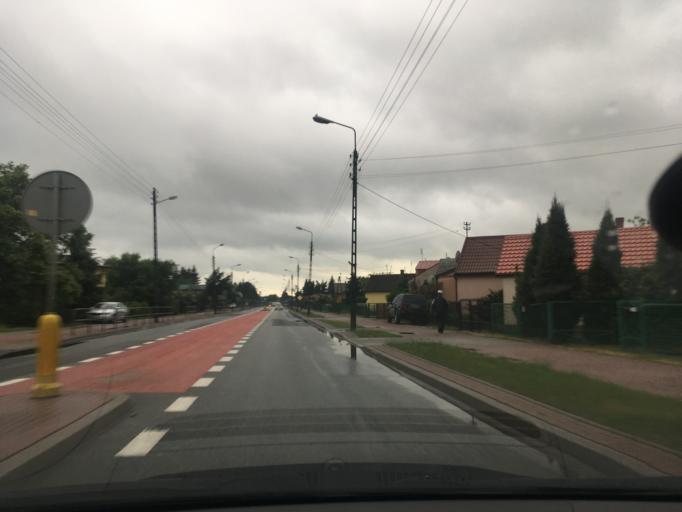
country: PL
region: Lublin Voivodeship
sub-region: Powiat rycki
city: Deblin
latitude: 51.5671
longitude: 21.8794
